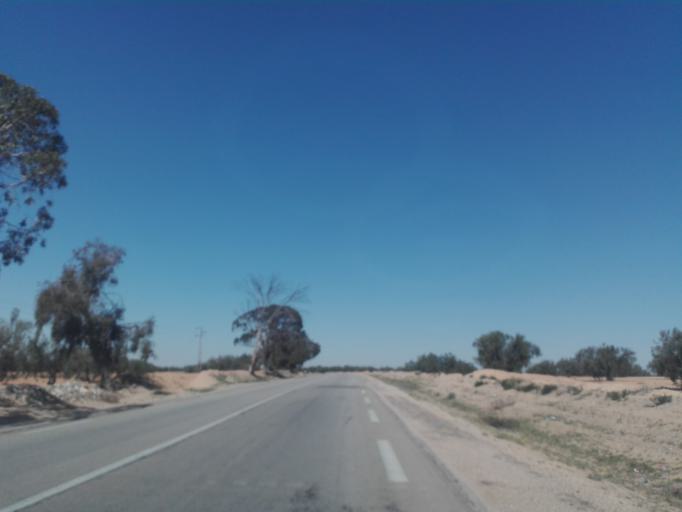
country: TN
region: Safaqis
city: Bi'r `Ali Bin Khalifah
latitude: 34.7560
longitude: 10.3295
